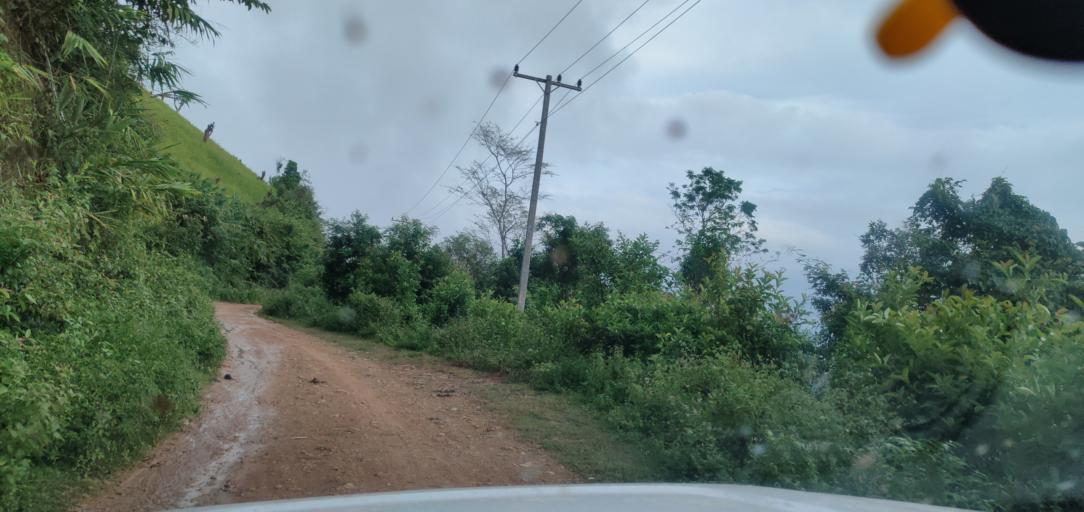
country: LA
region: Phongsali
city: Phongsali
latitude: 21.4482
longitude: 102.2869
